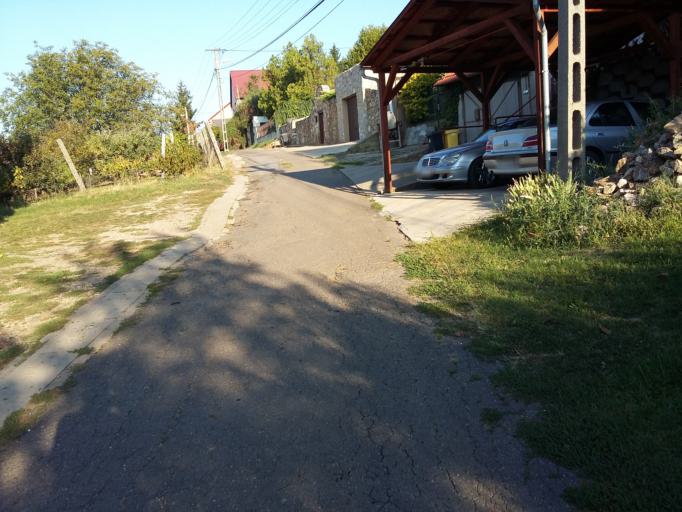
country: HU
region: Borsod-Abauj-Zemplen
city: Bekecs
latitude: 48.1527
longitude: 21.1674
